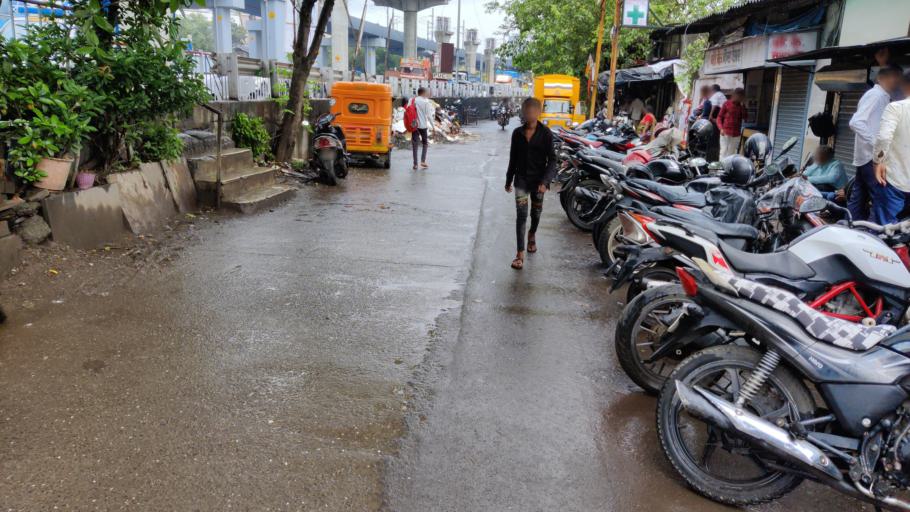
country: IN
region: Maharashtra
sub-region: Mumbai Suburban
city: Borivli
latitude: 19.2469
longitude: 72.8652
